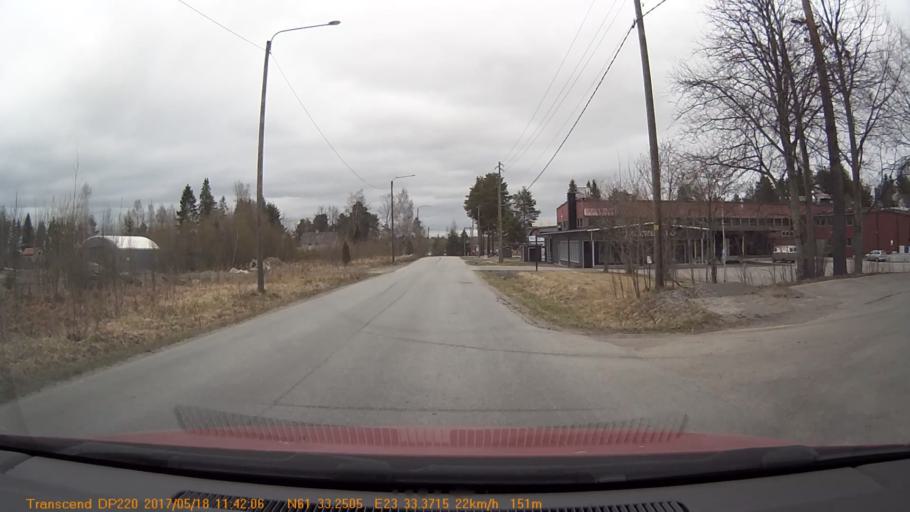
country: FI
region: Pirkanmaa
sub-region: Tampere
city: Yloejaervi
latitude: 61.5543
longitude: 23.5563
